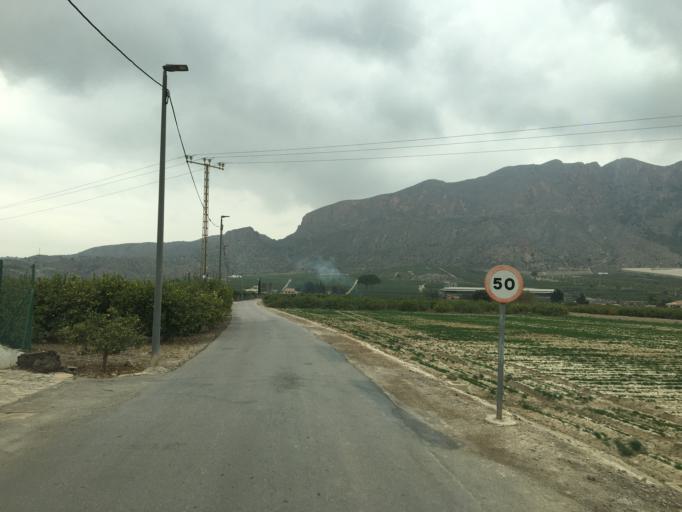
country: ES
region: Murcia
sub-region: Murcia
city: Santomera
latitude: 38.0702
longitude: -1.0275
